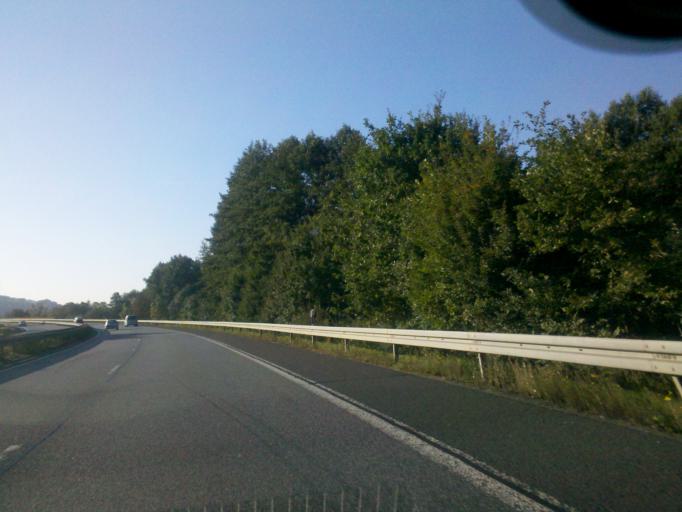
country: DE
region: Hesse
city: Herborn
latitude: 50.7097
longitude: 8.3039
